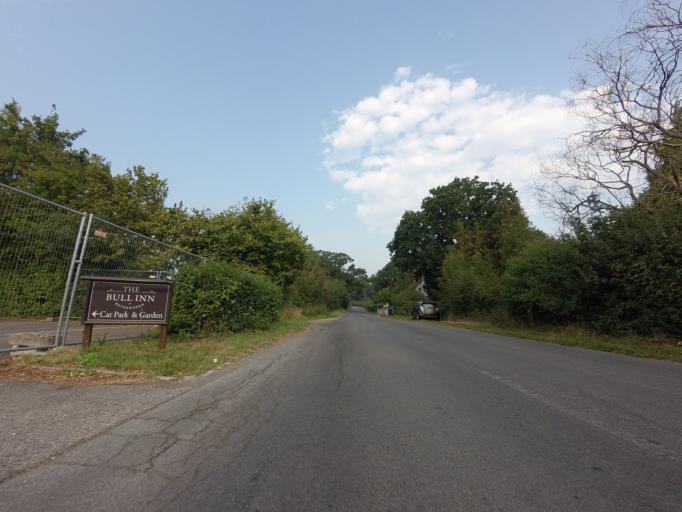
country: GB
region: England
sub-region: Kent
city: Tenterden
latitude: 51.1258
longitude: 0.7479
